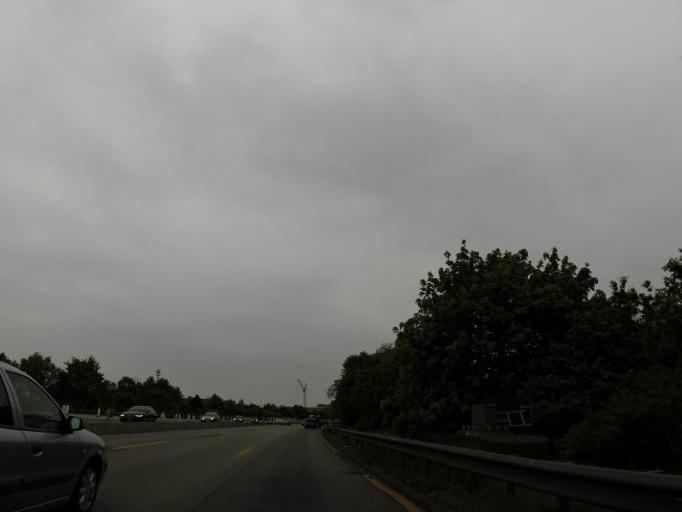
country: DE
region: Hamburg
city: Stellingen
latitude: 53.5814
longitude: 9.9150
